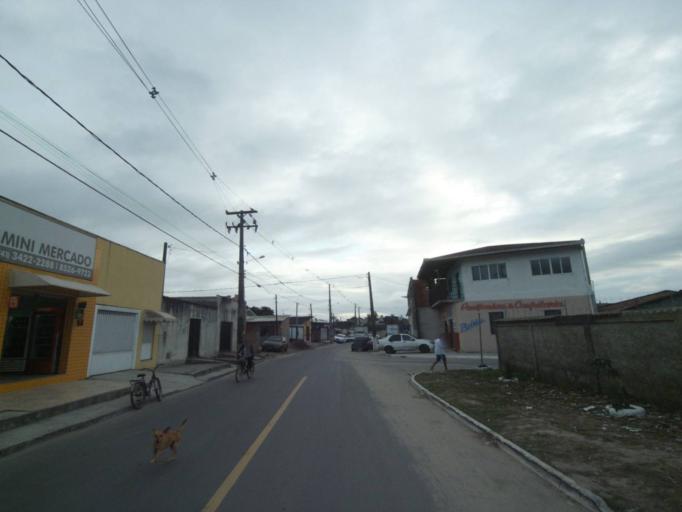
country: BR
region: Parana
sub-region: Paranagua
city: Paranagua
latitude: -25.5313
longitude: -48.5434
